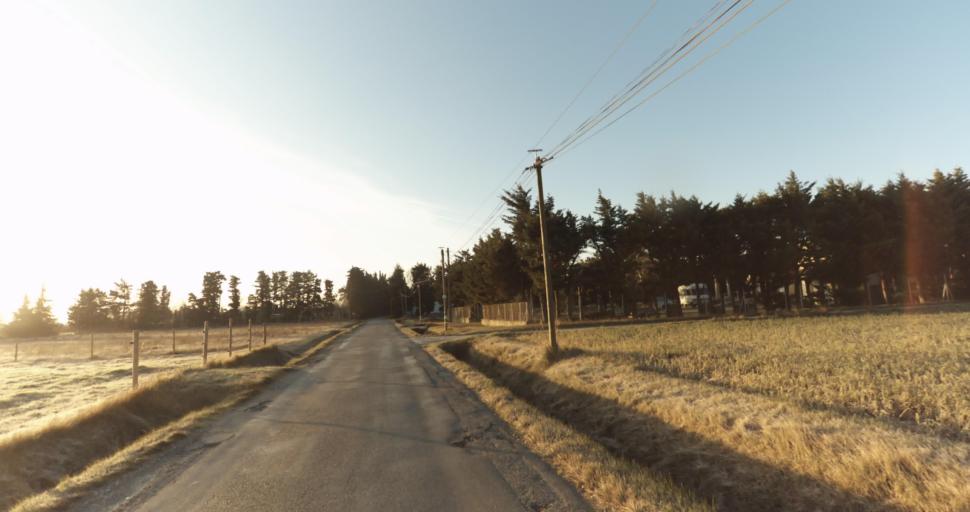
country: FR
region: Provence-Alpes-Cote d'Azur
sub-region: Departement des Bouches-du-Rhone
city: Barbentane
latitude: 43.8902
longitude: 4.7718
